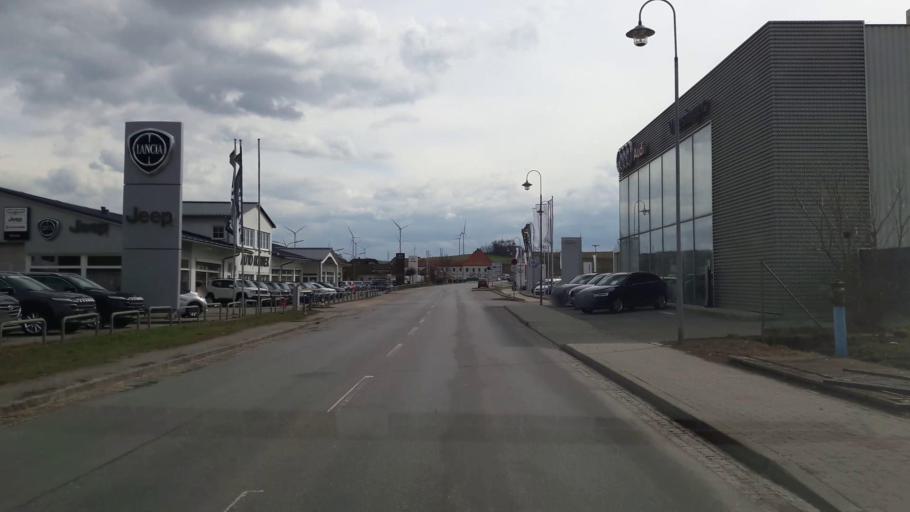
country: AT
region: Lower Austria
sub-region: Politischer Bezirk Mistelbach
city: Mistelbach
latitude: 48.5591
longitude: 16.5620
